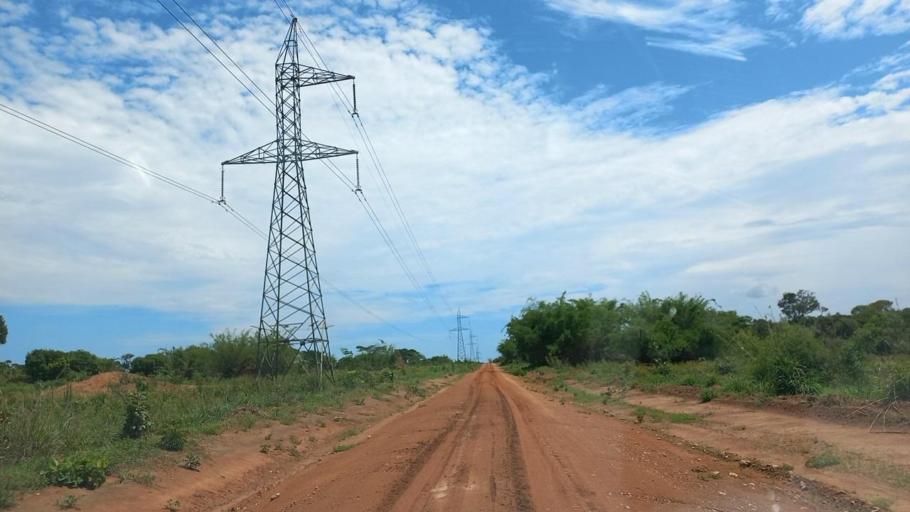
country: ZM
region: Copperbelt
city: Kitwe
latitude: -12.8222
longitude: 28.3519
